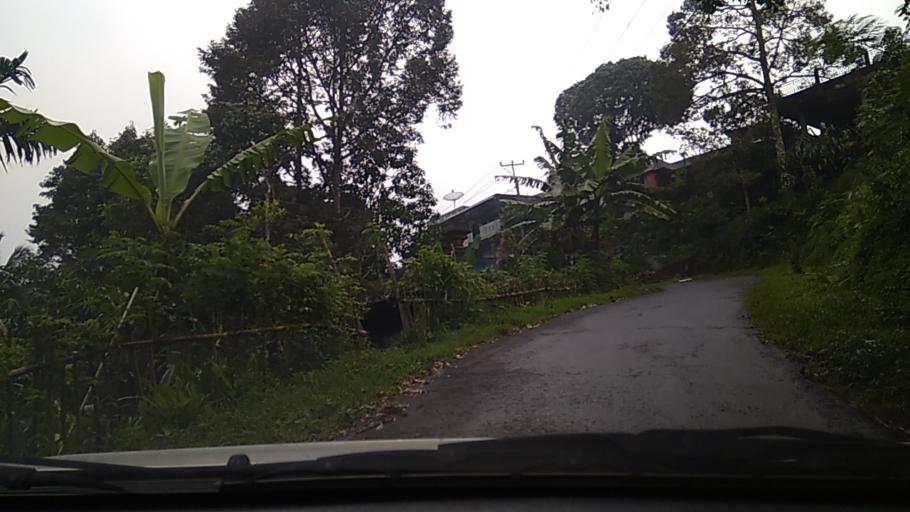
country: ID
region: Bali
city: Banjar Padangbulia
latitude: -8.1937
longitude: 115.1839
